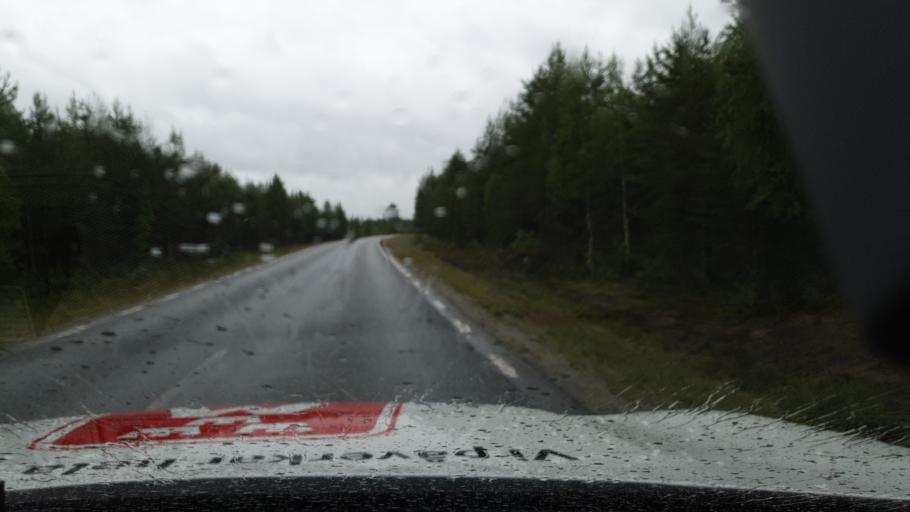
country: SE
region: Vaesterbotten
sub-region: Asele Kommun
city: Asele
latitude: 64.1863
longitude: 17.3474
